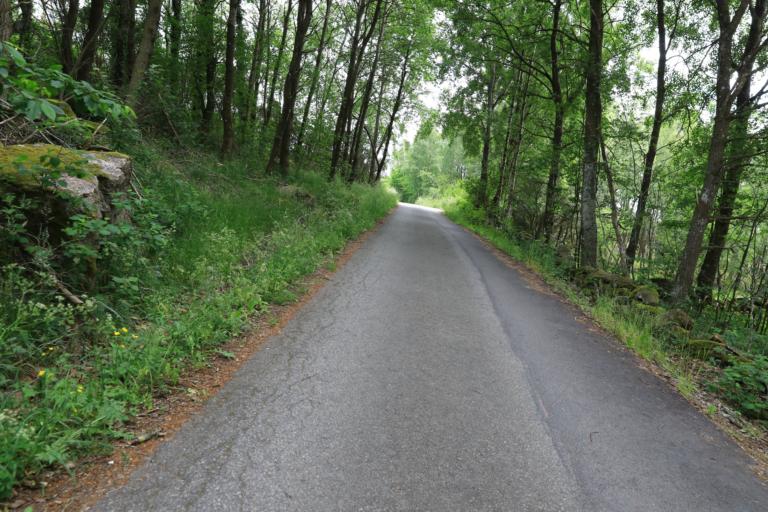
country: SE
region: Halland
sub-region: Varbergs Kommun
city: Varberg
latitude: 57.1661
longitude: 12.2498
